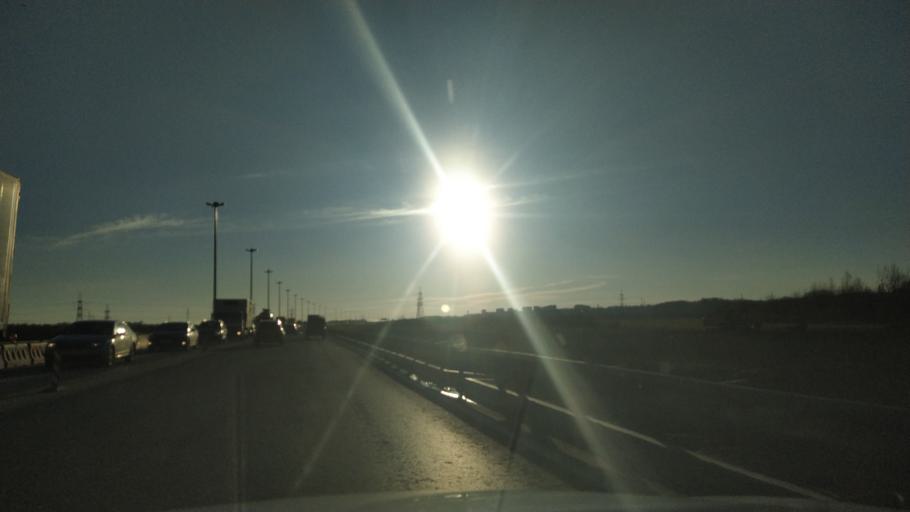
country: RU
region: Leningrad
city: Parnas
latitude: 60.0952
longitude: 30.3302
